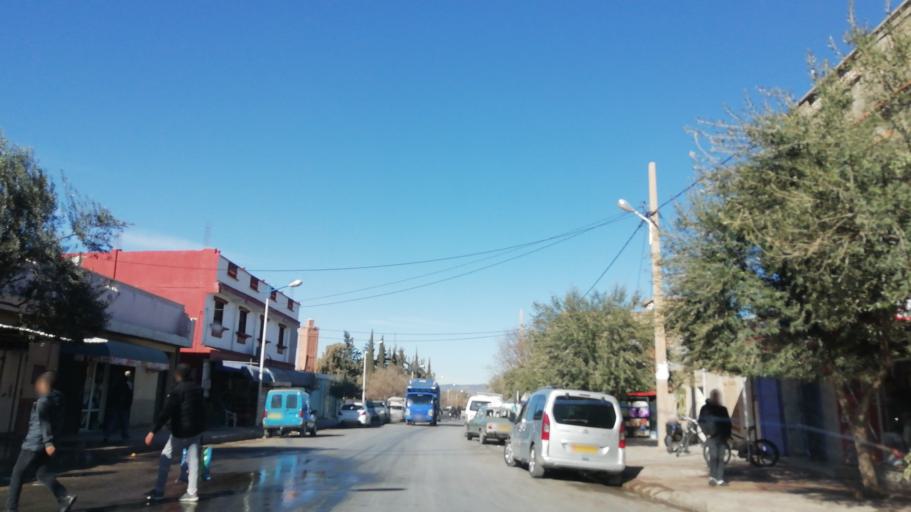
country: DZ
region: Tlemcen
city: Sebdou
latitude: 34.6485
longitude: -1.3237
